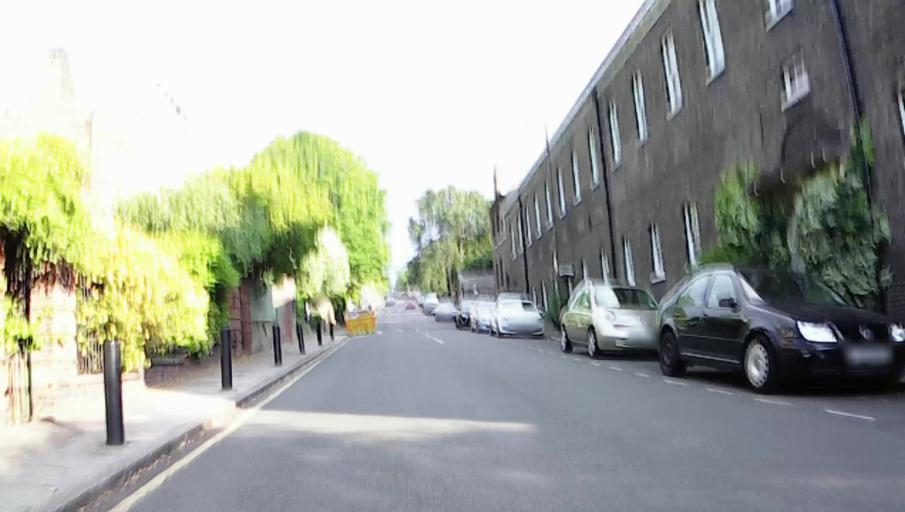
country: GB
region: England
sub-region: Greater London
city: Blackheath
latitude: 51.4821
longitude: 0.0021
